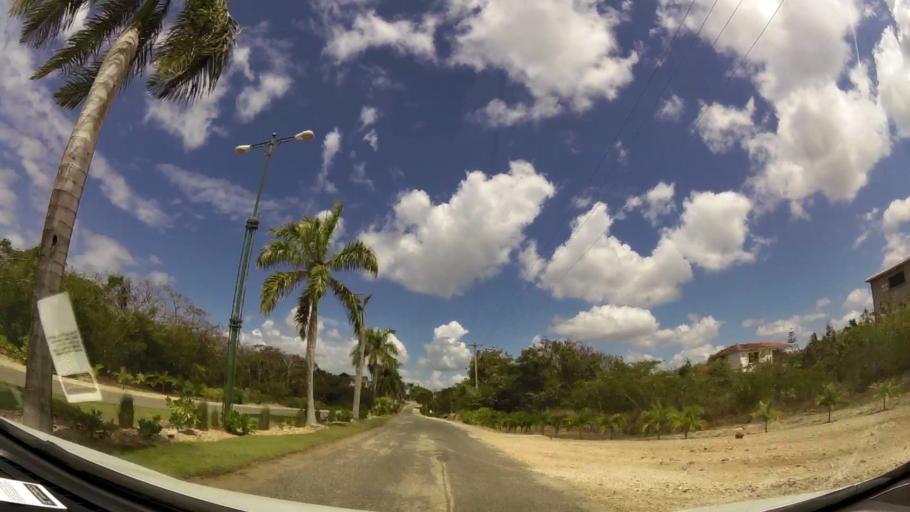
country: DO
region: Santo Domingo
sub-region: Santo Domingo
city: Boca Chica
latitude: 18.4649
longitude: -69.6540
